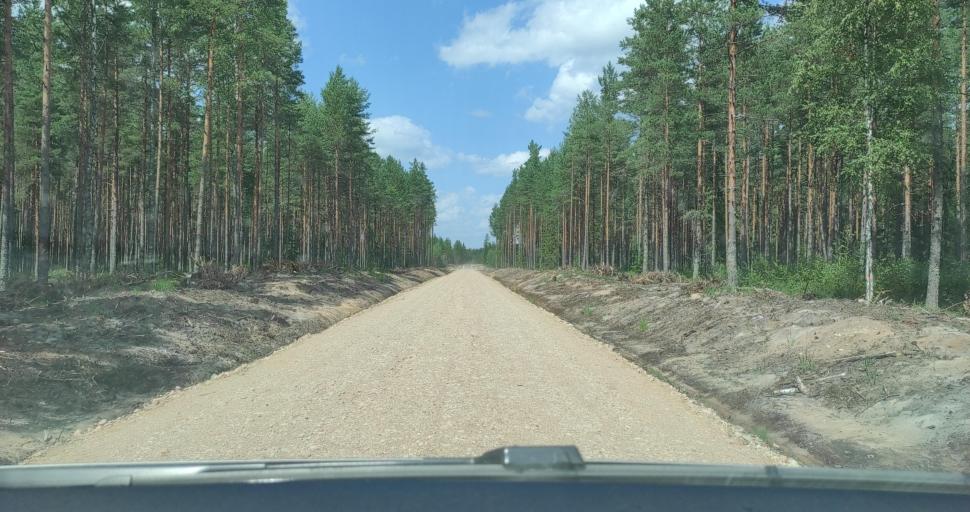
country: LV
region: Kuldigas Rajons
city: Kuldiga
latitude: 57.0552
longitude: 22.1903
